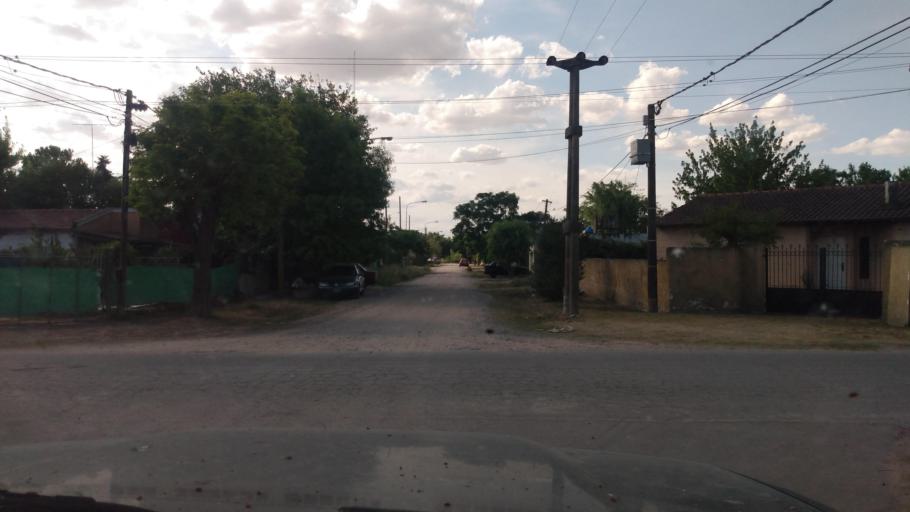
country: AR
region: Buenos Aires
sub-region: Partido de Lujan
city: Lujan
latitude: -34.5484
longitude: -59.1060
